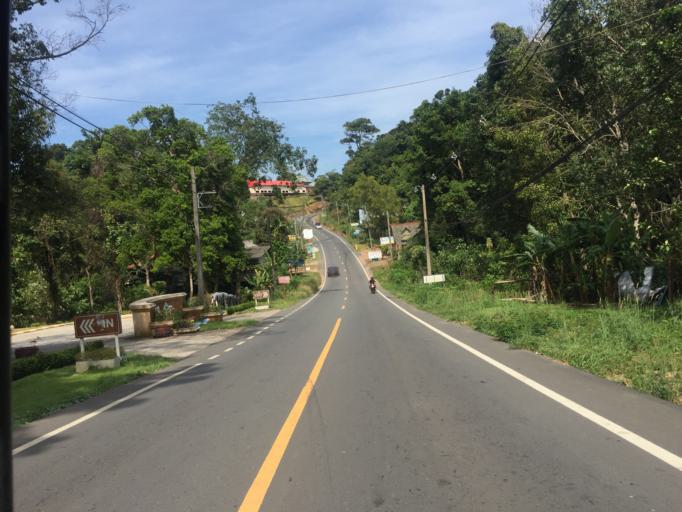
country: TH
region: Trat
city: Laem Ngop
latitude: 12.1378
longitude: 102.2765
